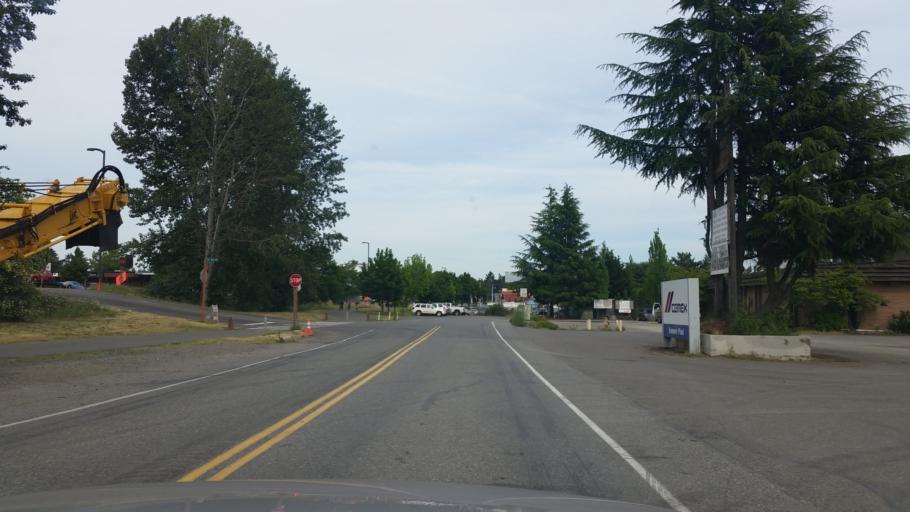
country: US
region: Washington
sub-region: King County
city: Kenmore
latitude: 47.7583
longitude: -122.2544
